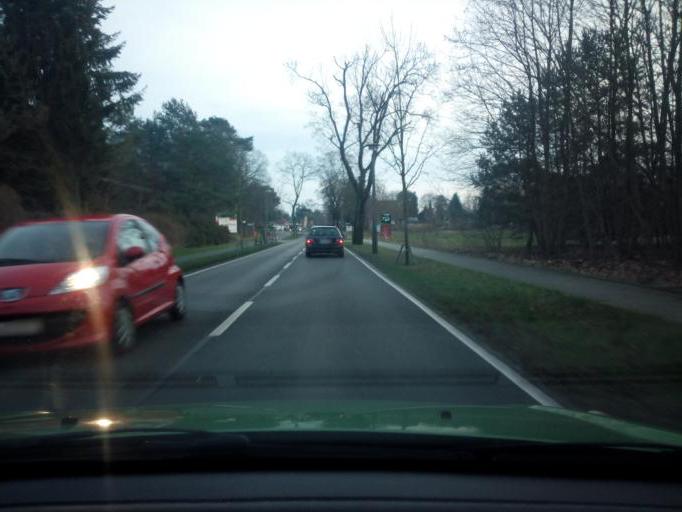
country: DE
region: Berlin
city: Muggelheim
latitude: 52.4166
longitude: 13.6541
